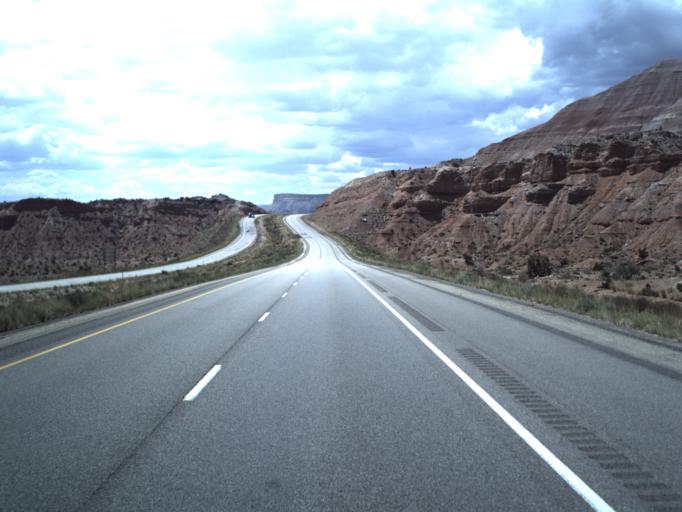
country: US
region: Utah
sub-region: Emery County
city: Ferron
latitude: 38.8294
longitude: -111.1387
